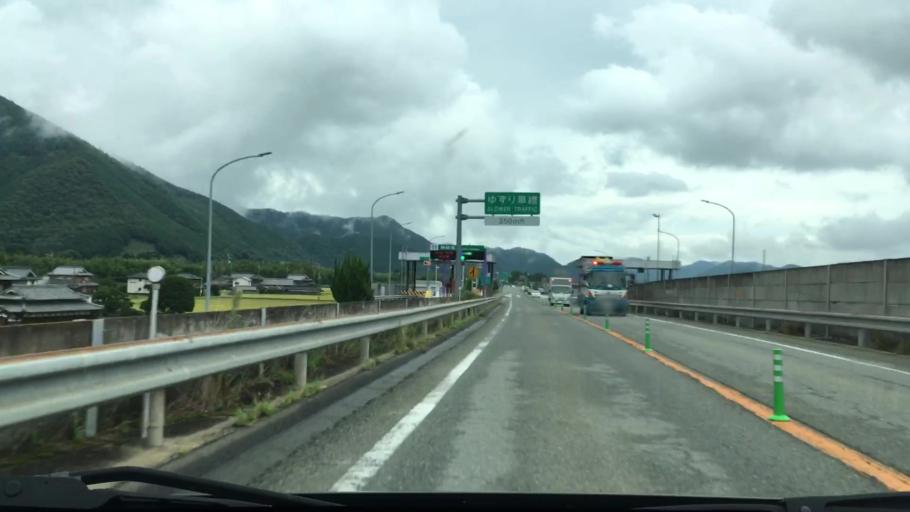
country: JP
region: Hyogo
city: Yamazakicho-nakabirose
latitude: 35.0566
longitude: 134.7637
